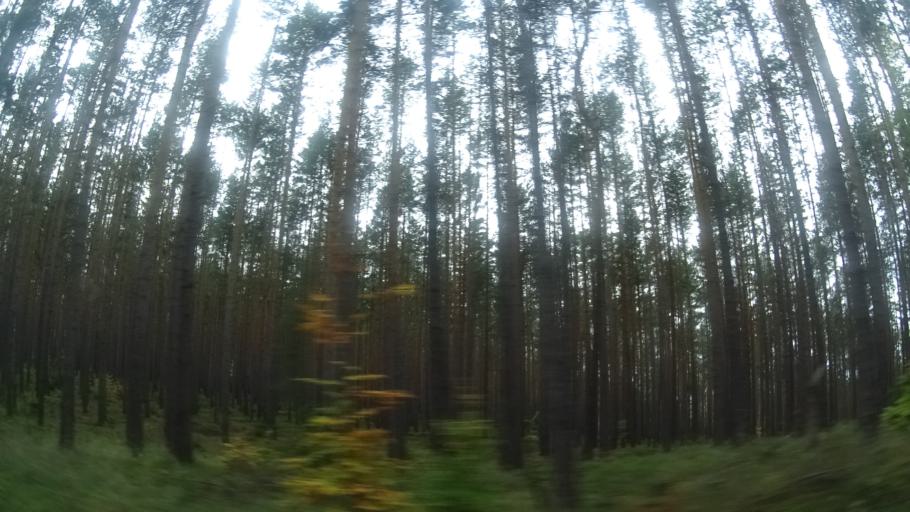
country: DE
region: Thuringia
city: Saalfeld
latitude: 50.6758
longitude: 11.3892
